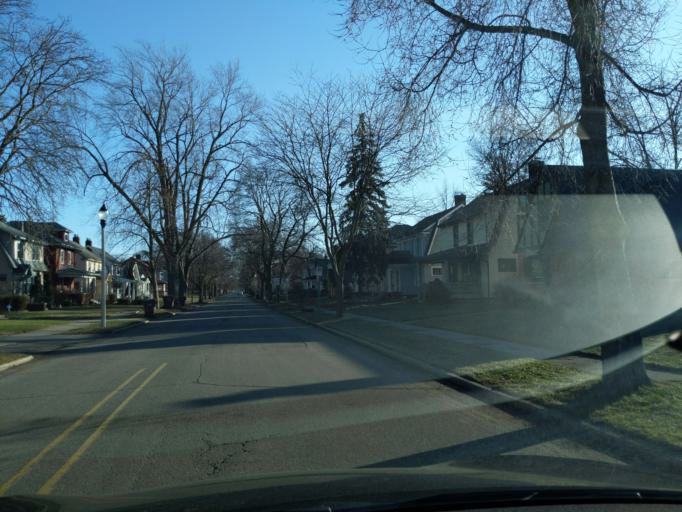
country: US
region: Michigan
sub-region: Ingham County
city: Lansing
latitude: 42.7407
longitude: -84.5728
